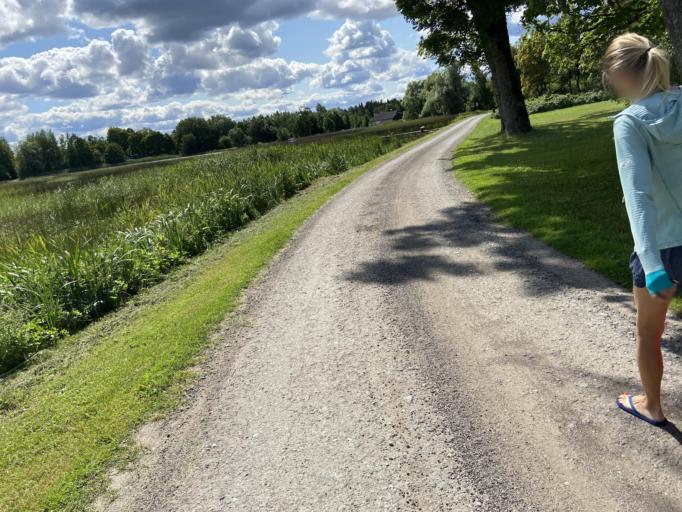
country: EE
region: Harju
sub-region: Keila linn
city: Keila
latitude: 59.1574
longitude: 24.4932
